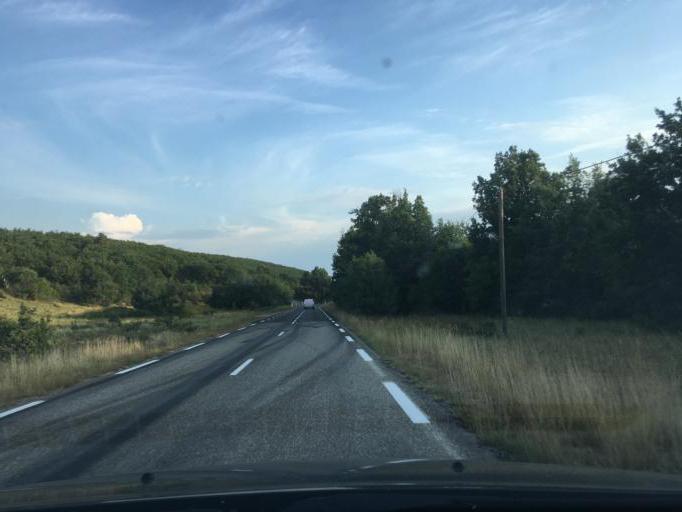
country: FR
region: Provence-Alpes-Cote d'Azur
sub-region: Departement du Var
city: Aups
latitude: 43.7271
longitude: 6.2212
